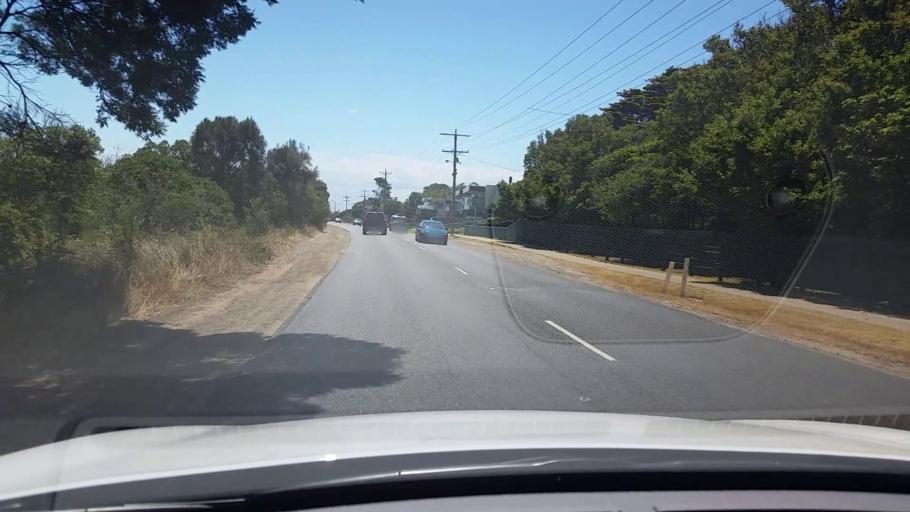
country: AU
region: Victoria
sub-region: Mornington Peninsula
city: Mount Martha
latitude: -38.2467
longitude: 145.0295
